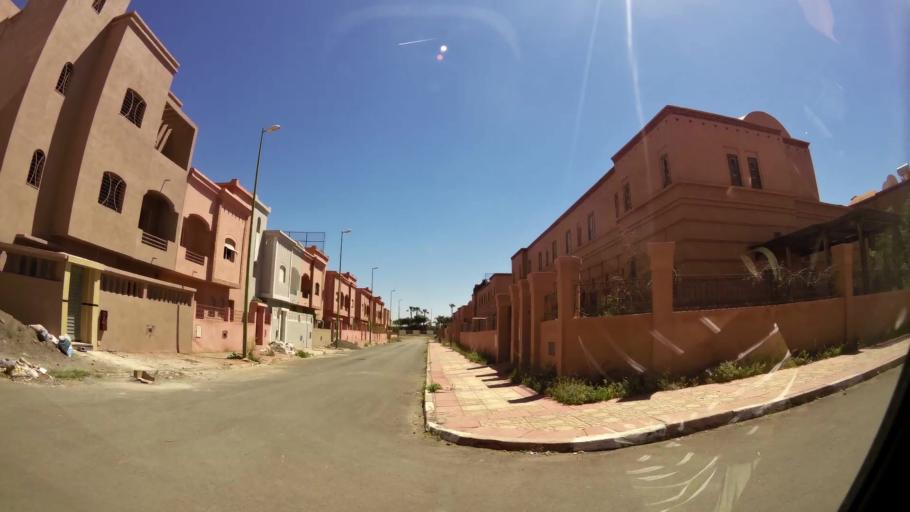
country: MA
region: Marrakech-Tensift-Al Haouz
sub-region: Marrakech
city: Marrakesh
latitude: 31.5704
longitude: -7.9827
